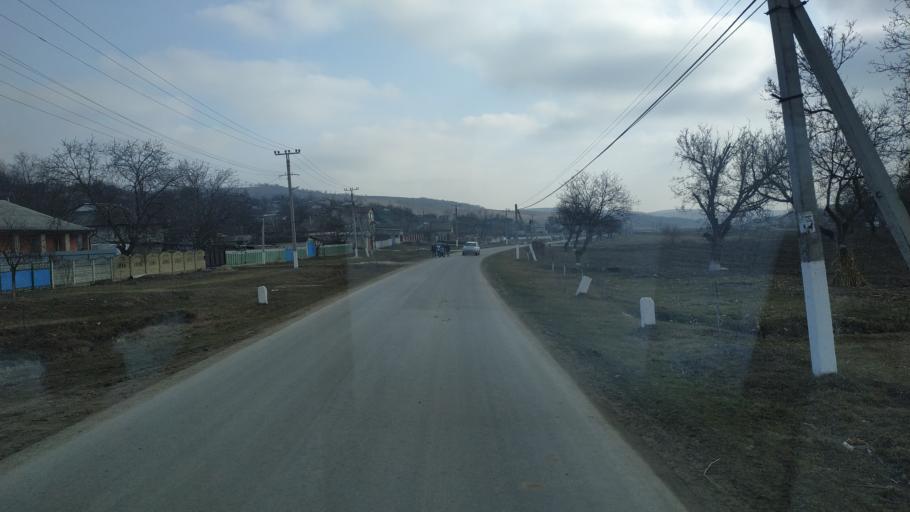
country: MD
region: Nisporeni
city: Nisporeni
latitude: 46.9395
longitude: 28.3270
